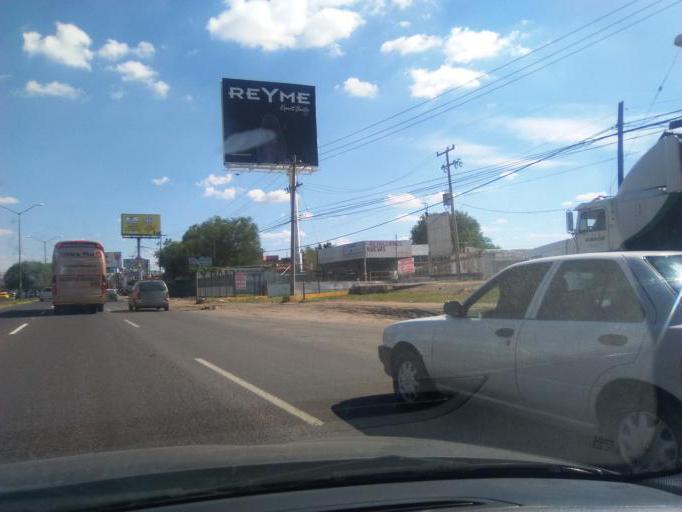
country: MX
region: Guanajuato
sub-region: Leon
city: Fraccionamiento Paraiso Real
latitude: 21.0876
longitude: -101.6175
